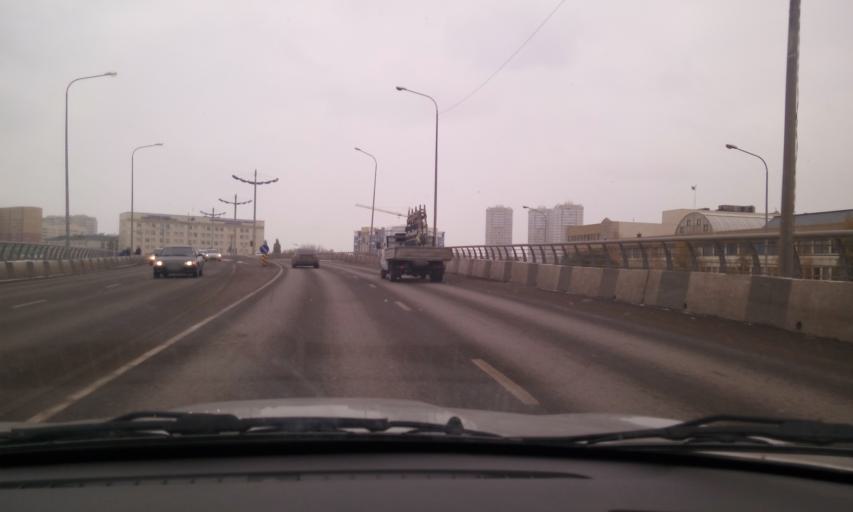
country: KZ
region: Astana Qalasy
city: Astana
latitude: 51.1568
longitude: 71.4668
